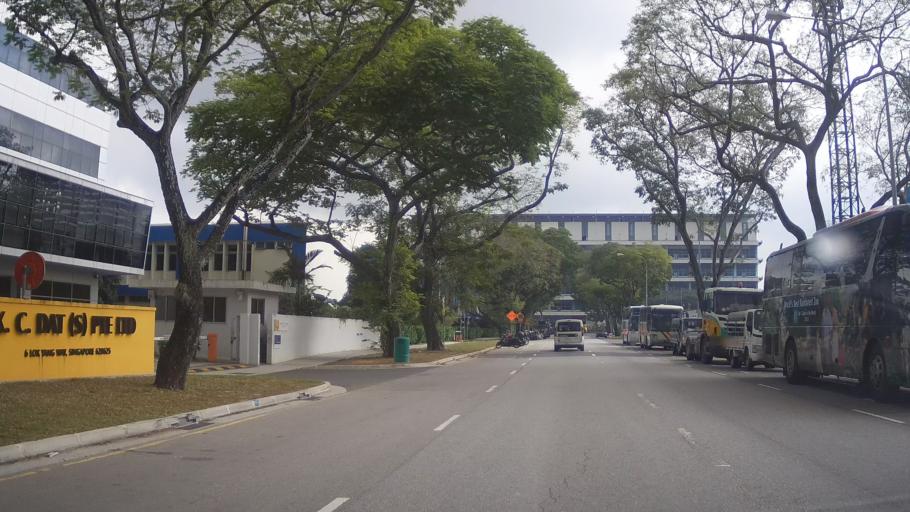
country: MY
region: Johor
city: Johor Bahru
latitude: 1.3246
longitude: 103.6939
